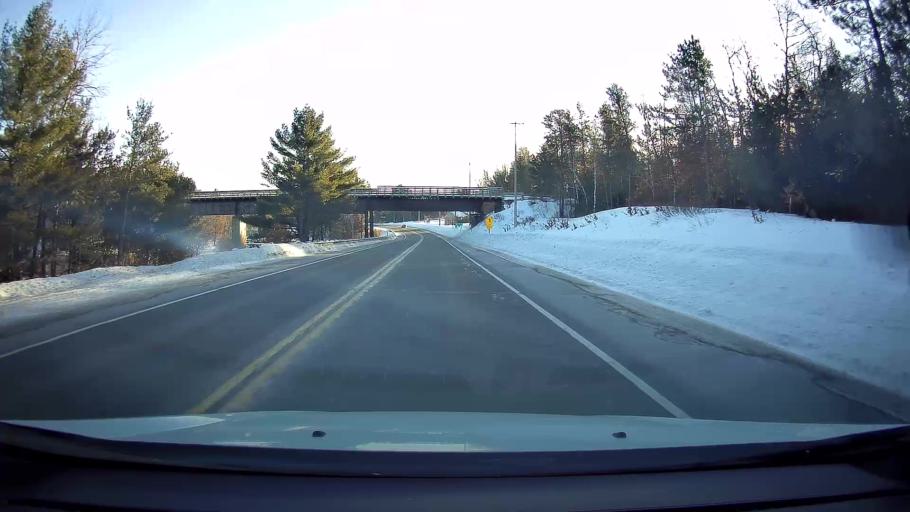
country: US
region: Wisconsin
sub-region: Washburn County
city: Spooner
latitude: 45.9053
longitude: -91.8193
